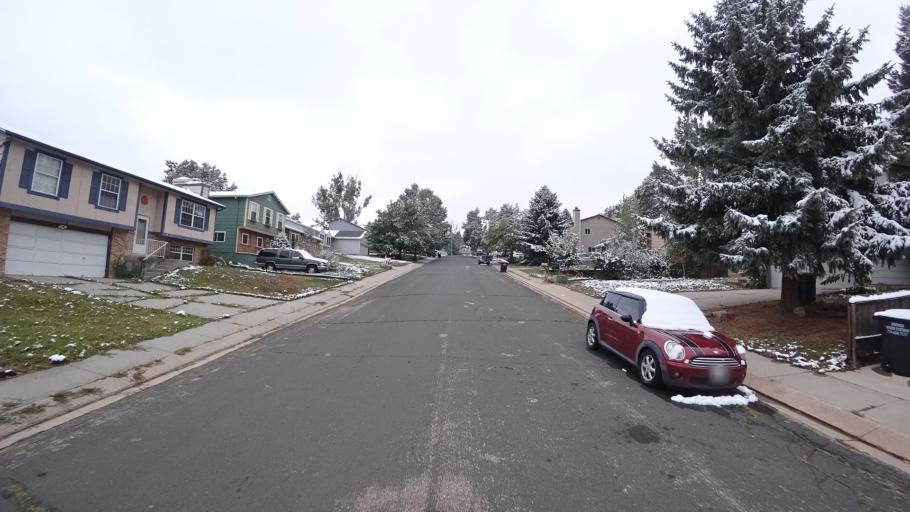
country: US
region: Colorado
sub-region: El Paso County
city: Cimarron Hills
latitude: 38.9282
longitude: -104.7686
